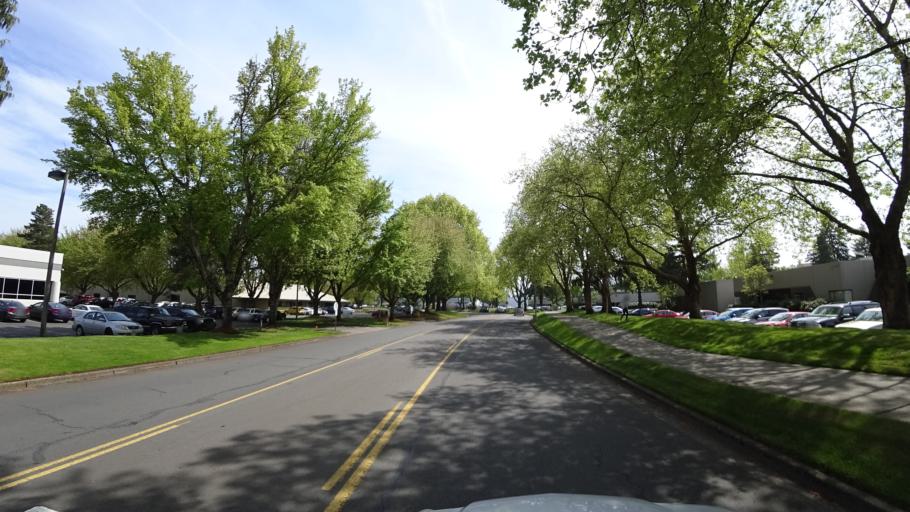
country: US
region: Oregon
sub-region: Washington County
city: Rockcreek
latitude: 45.5286
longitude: -122.9308
